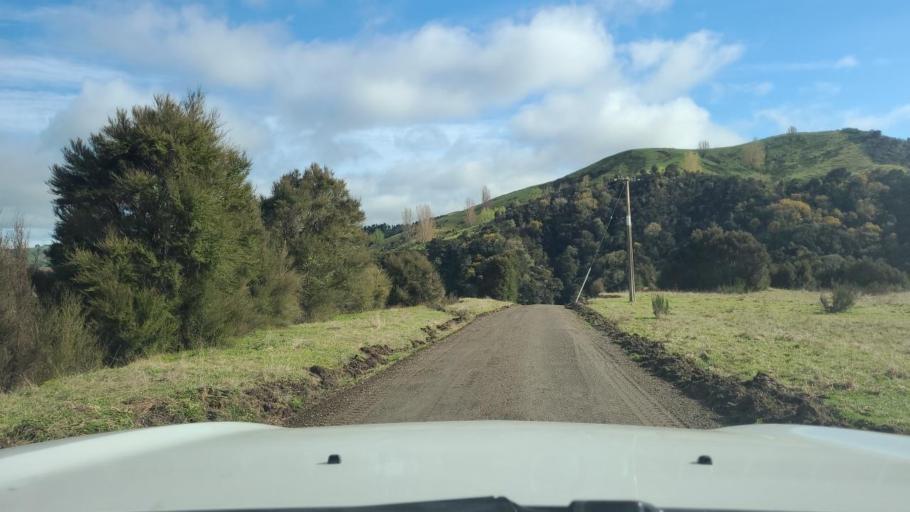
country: NZ
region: Wellington
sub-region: South Wairarapa District
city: Waipawa
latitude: -41.2346
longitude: 175.7039
